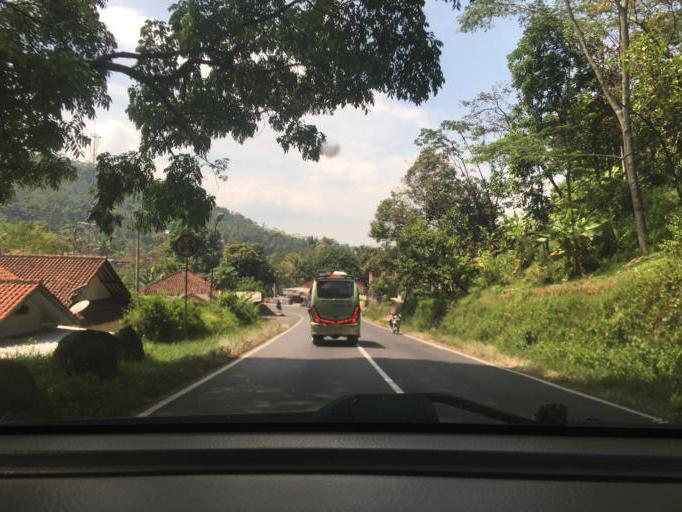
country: ID
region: West Java
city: Tagog
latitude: -7.1170
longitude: 108.1271
